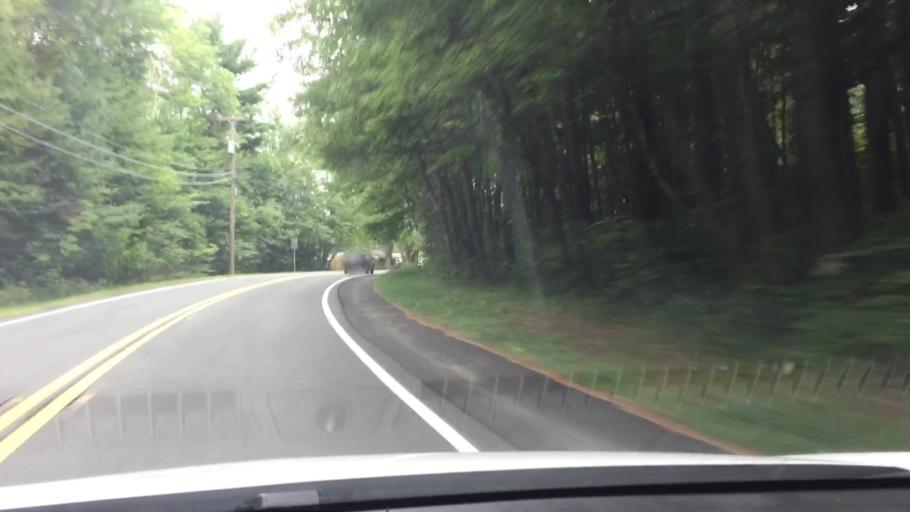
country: US
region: Massachusetts
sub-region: Berkshire County
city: Becket
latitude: 42.3750
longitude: -73.1165
